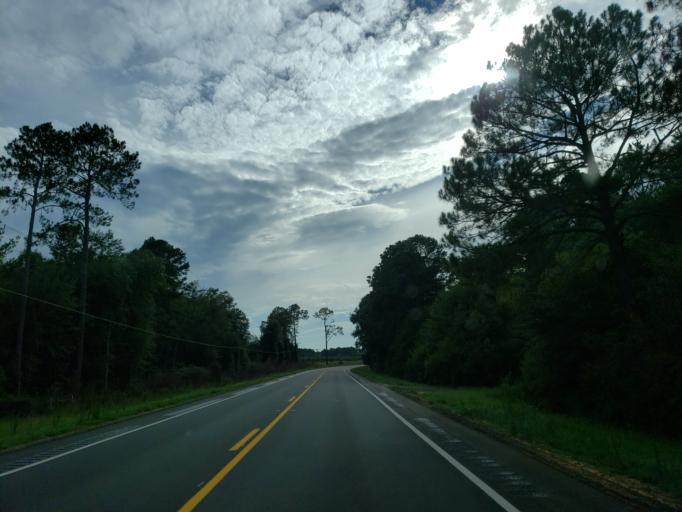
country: US
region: Georgia
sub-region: Irwin County
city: Ocilla
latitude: 31.5636
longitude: -83.3244
